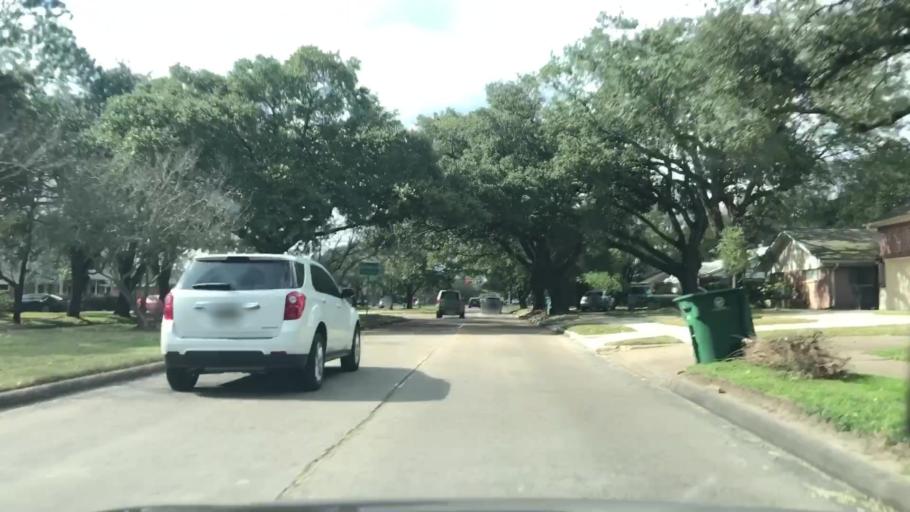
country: US
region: Texas
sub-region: Harris County
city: Bellaire
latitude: 29.6892
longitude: -95.4825
